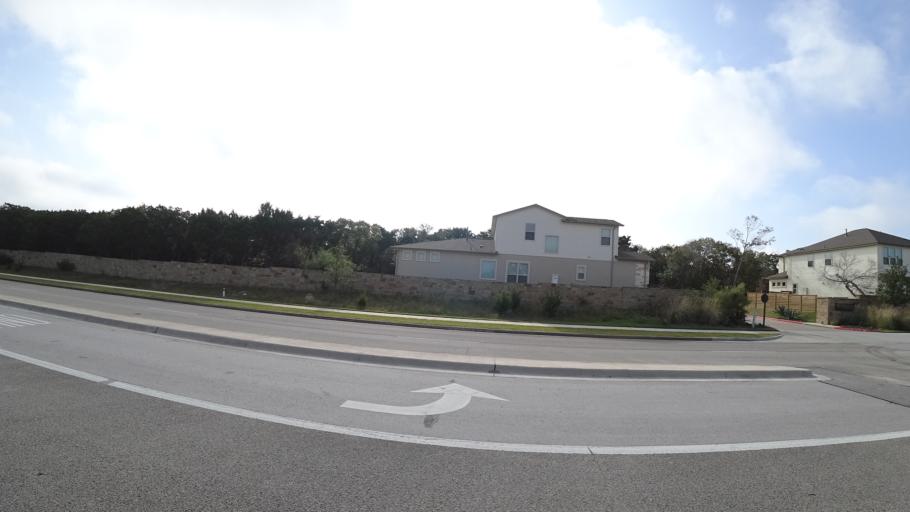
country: US
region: Texas
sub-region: Williamson County
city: Anderson Mill
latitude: 30.4020
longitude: -97.8418
